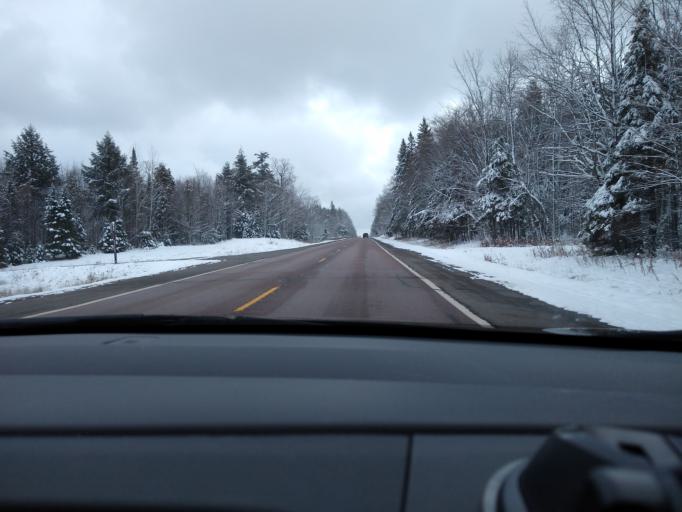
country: US
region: Wisconsin
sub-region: Vilas County
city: Eagle River
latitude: 46.2230
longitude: -89.0610
